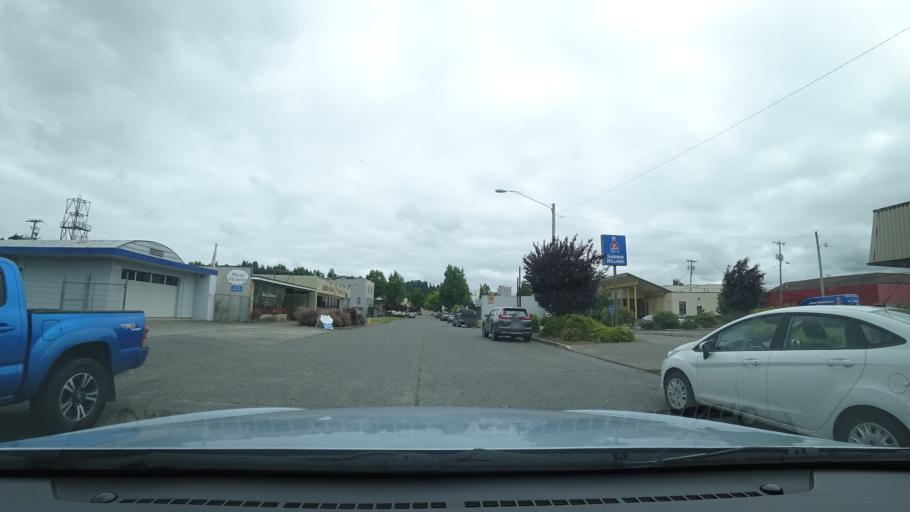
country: US
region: Oregon
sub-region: Coos County
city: Coos Bay
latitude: 43.3645
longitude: -124.2147
